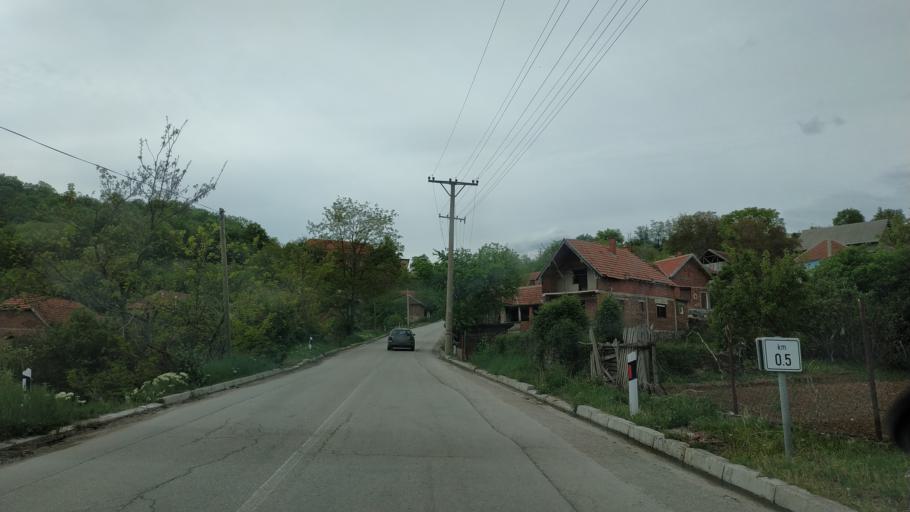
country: RS
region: Central Serbia
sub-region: Nisavski Okrug
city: Aleksinac
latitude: 43.6365
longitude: 21.7161
